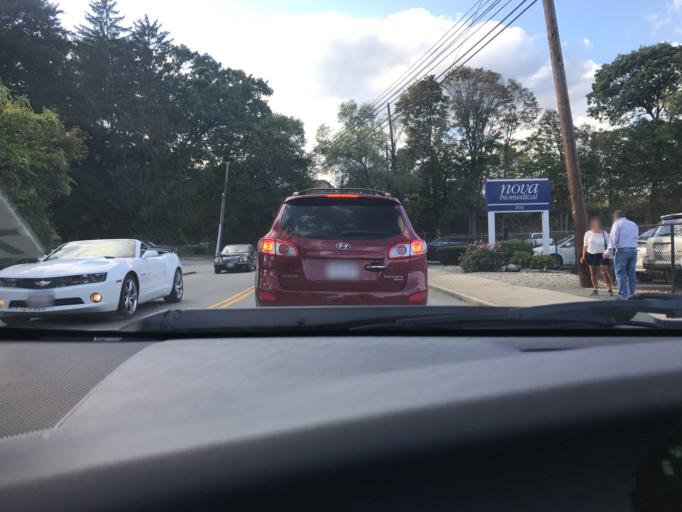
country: US
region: Massachusetts
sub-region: Middlesex County
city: Waltham
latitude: 42.3692
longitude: -71.2445
